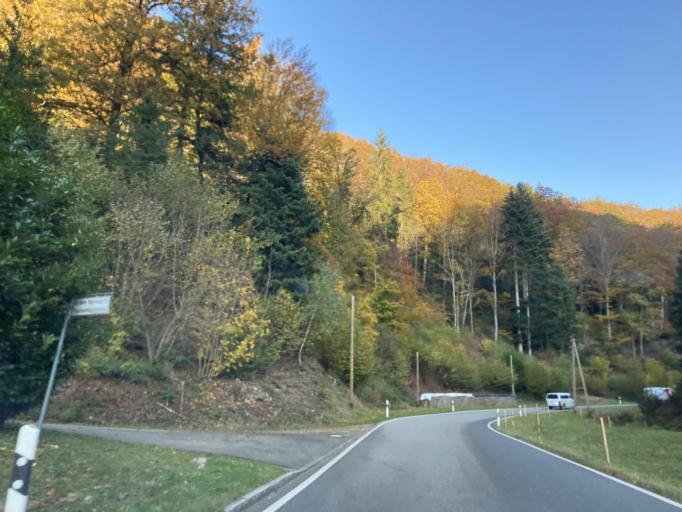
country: DE
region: Baden-Wuerttemberg
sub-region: Freiburg Region
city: Breitnau
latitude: 47.9708
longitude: 8.0706
